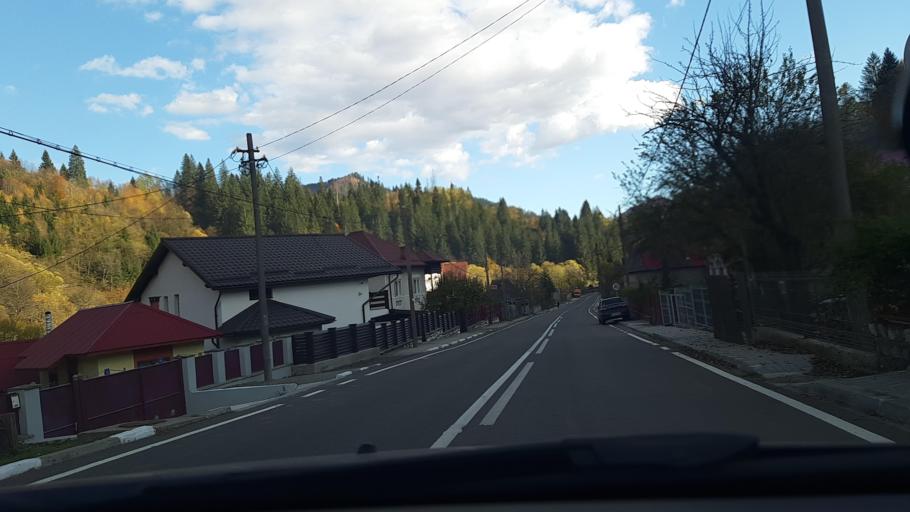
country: RO
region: Valcea
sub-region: Comuna Voineasa
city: Voineasa
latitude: 45.4257
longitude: 23.9490
